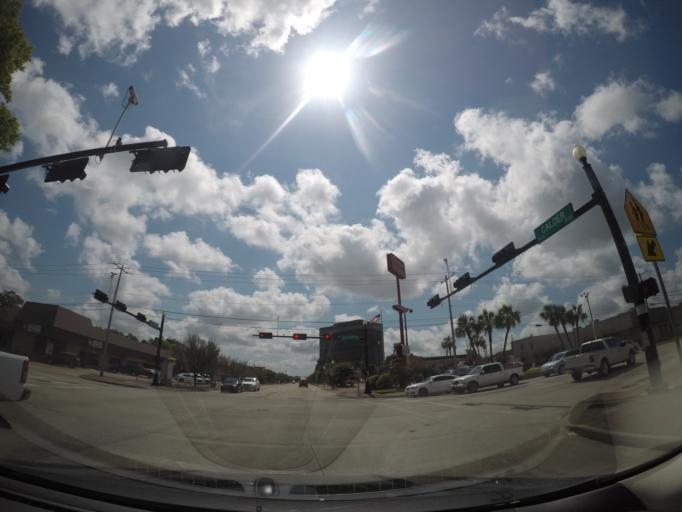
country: US
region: Texas
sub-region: Jefferson County
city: Beaumont
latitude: 30.0856
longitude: -94.1300
